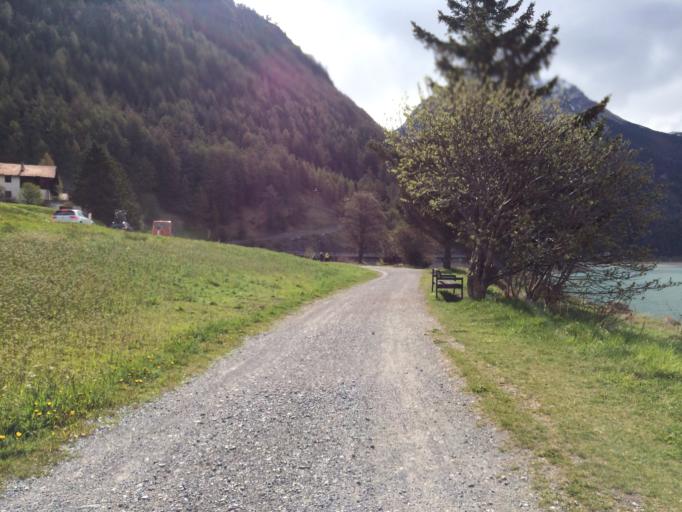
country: IT
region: Trentino-Alto Adige
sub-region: Bolzano
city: Curon Venosta
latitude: 46.8186
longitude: 10.5267
